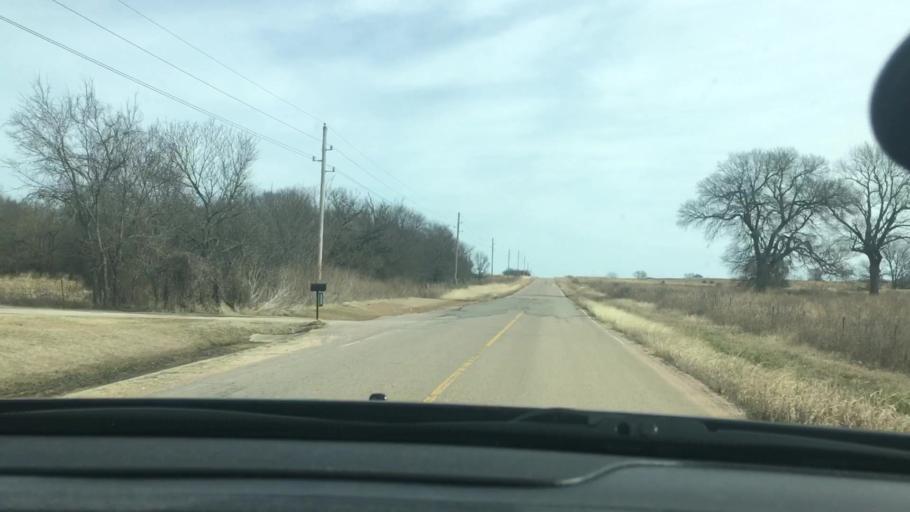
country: US
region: Oklahoma
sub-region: Murray County
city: Sulphur
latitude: 34.4049
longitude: -96.8971
